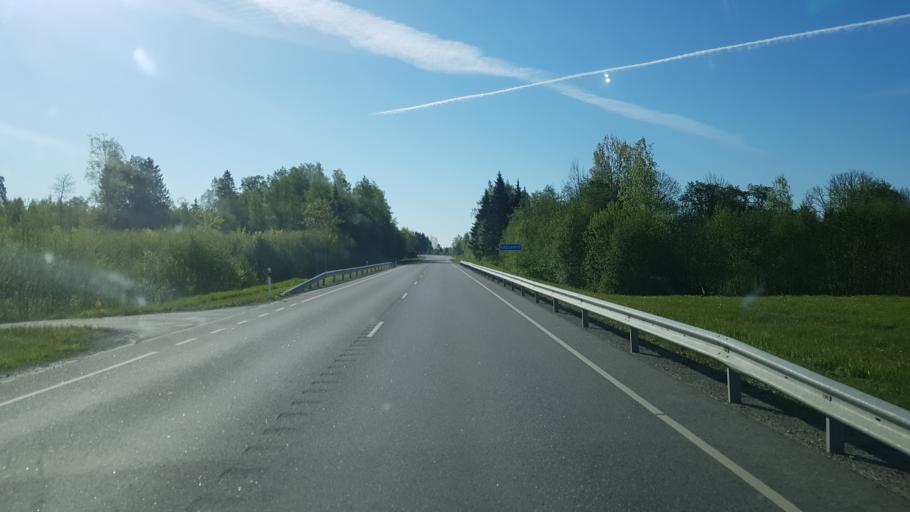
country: EE
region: Paernumaa
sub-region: Vaendra vald (alev)
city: Vandra
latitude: 58.6683
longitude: 25.1411
